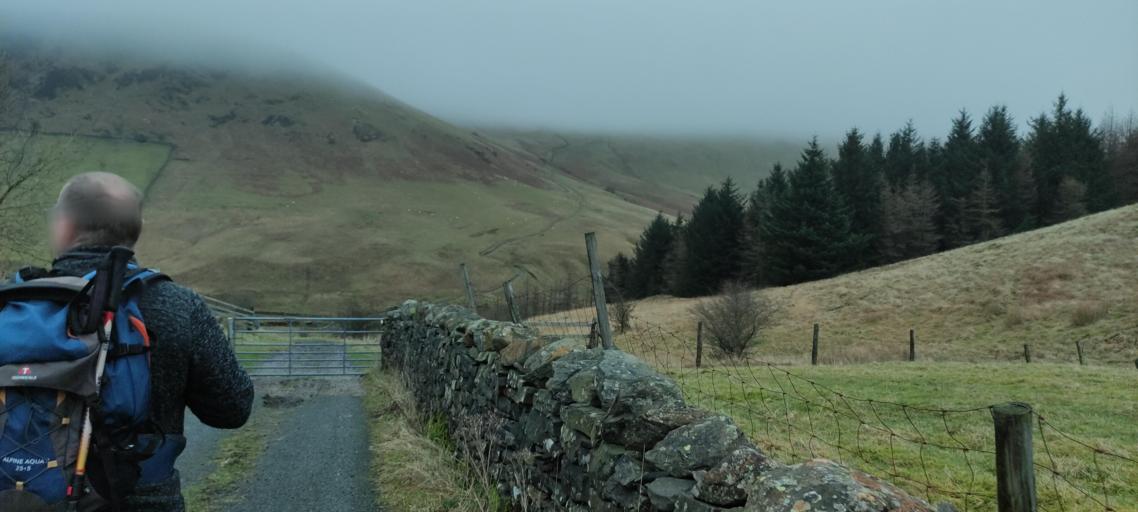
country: GB
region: England
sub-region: Cumbria
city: Kendal
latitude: 54.4252
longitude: -2.6904
